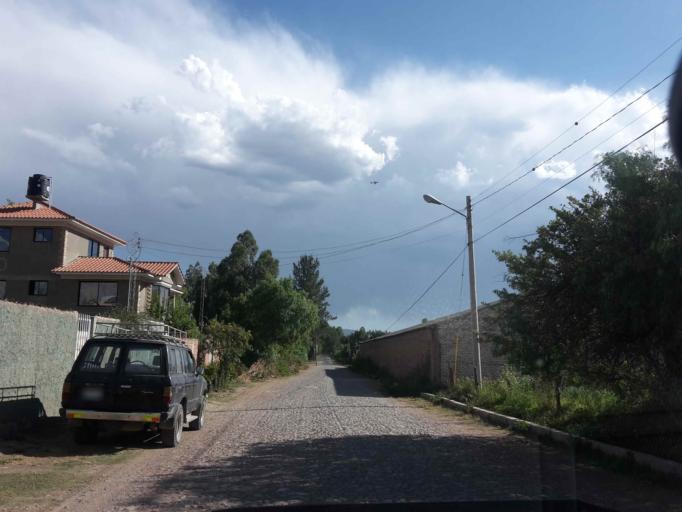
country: BO
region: Cochabamba
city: Cochabamba
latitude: -17.3565
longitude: -66.2208
